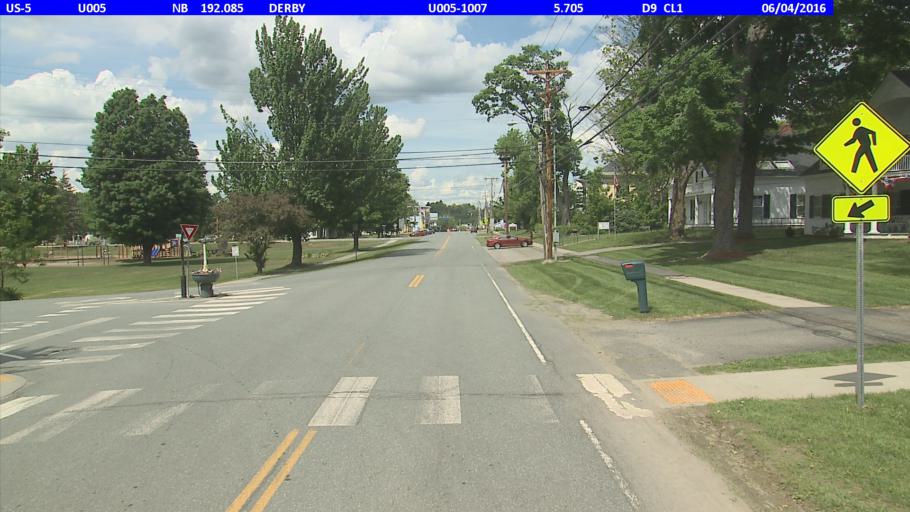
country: US
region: Vermont
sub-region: Orleans County
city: Newport
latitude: 45.0027
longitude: -72.1014
